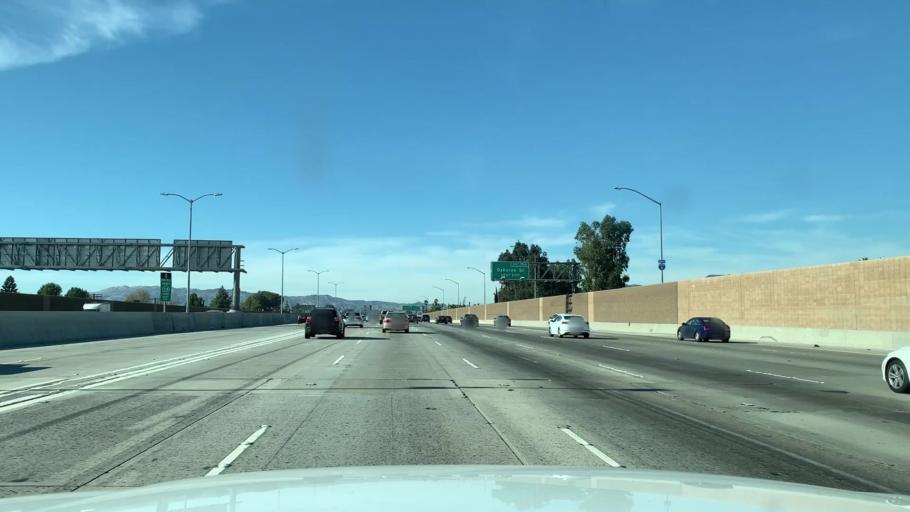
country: US
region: California
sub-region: Los Angeles County
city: San Fernando
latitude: 34.2388
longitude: -118.4159
